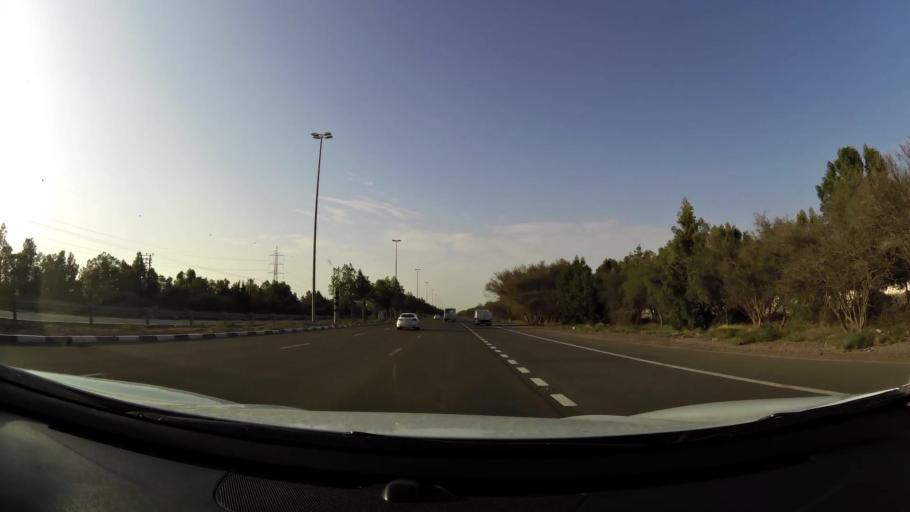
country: AE
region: Abu Dhabi
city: Al Ain
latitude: 24.1317
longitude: 55.8192
